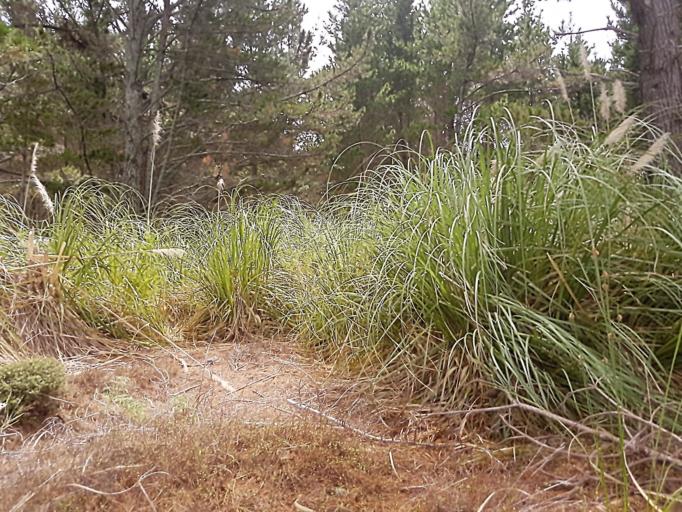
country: NZ
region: Bay of Plenty
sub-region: Tauranga City
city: Tauranga
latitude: -37.6424
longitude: 176.1467
